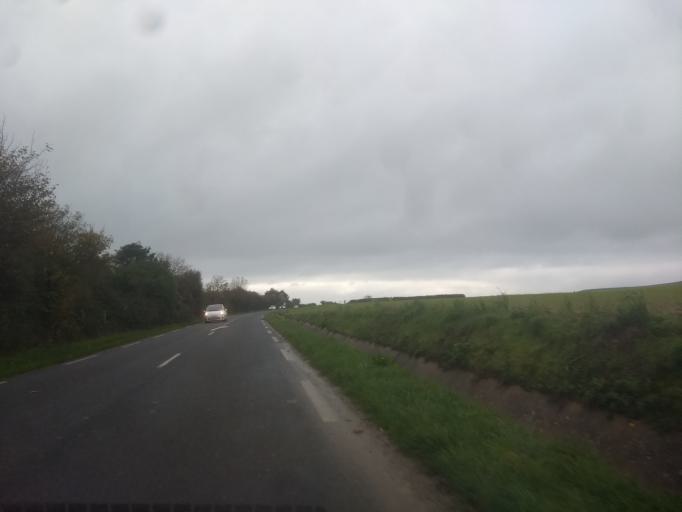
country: FR
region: Nord-Pas-de-Calais
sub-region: Departement du Pas-de-Calais
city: Wissant
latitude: 50.8989
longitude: 1.6840
